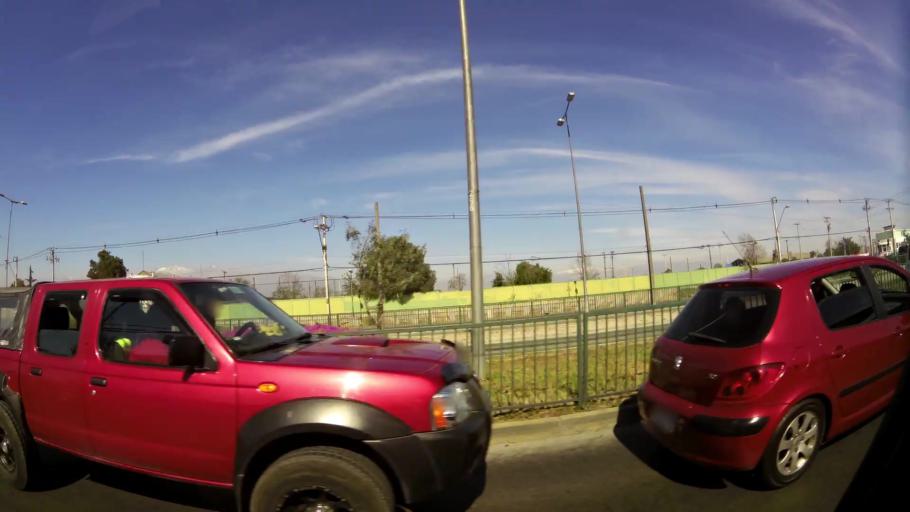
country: CL
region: Santiago Metropolitan
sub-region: Provincia de Santiago
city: Lo Prado
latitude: -33.4928
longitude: -70.7041
